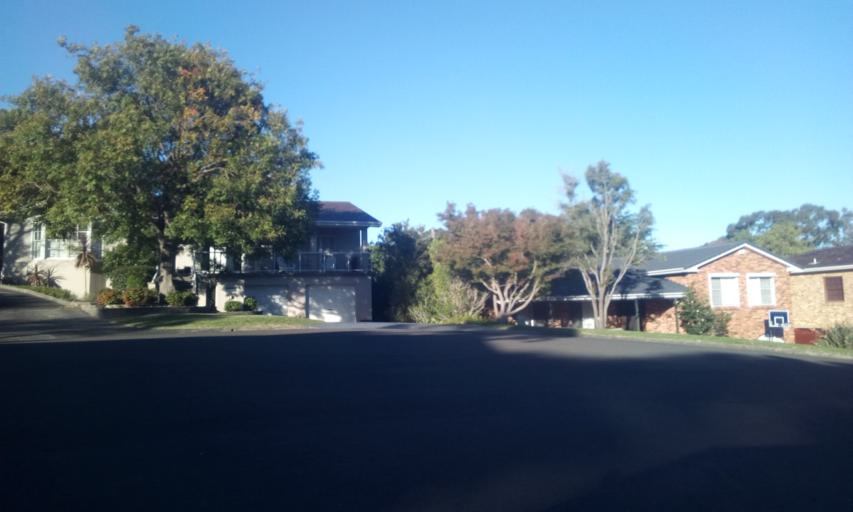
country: AU
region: New South Wales
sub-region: Wollongong
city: Mount Keira
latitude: -34.4217
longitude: 150.8478
